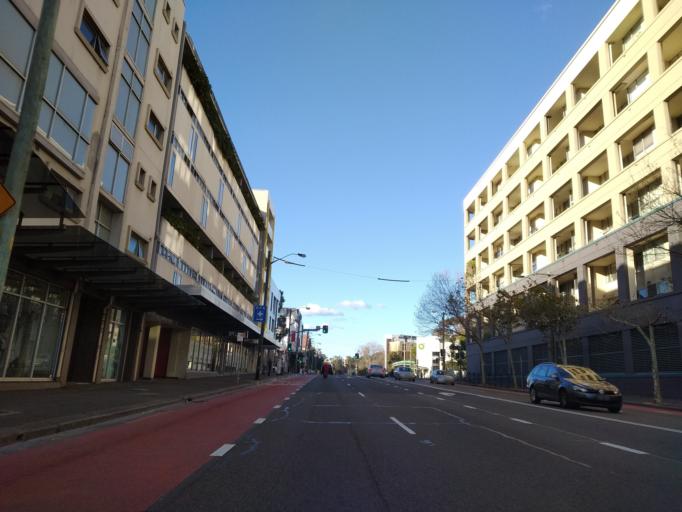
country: AU
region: New South Wales
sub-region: Marrickville
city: Camperdown
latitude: -33.8864
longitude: 151.1782
